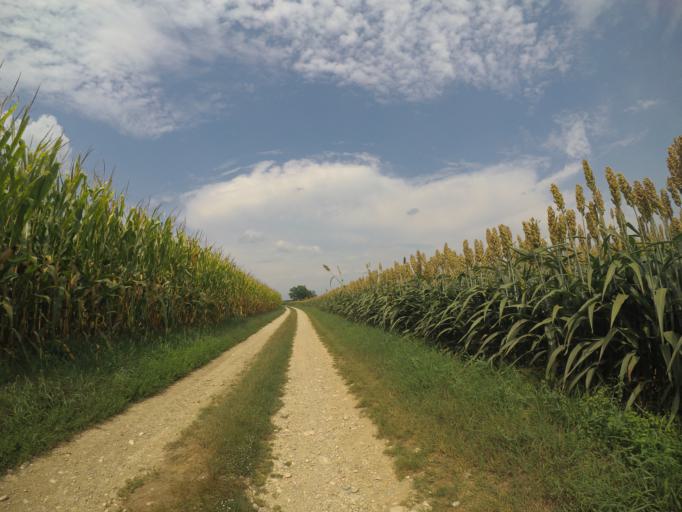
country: IT
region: Friuli Venezia Giulia
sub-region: Provincia di Udine
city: Bertiolo
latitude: 45.9624
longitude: 13.0682
